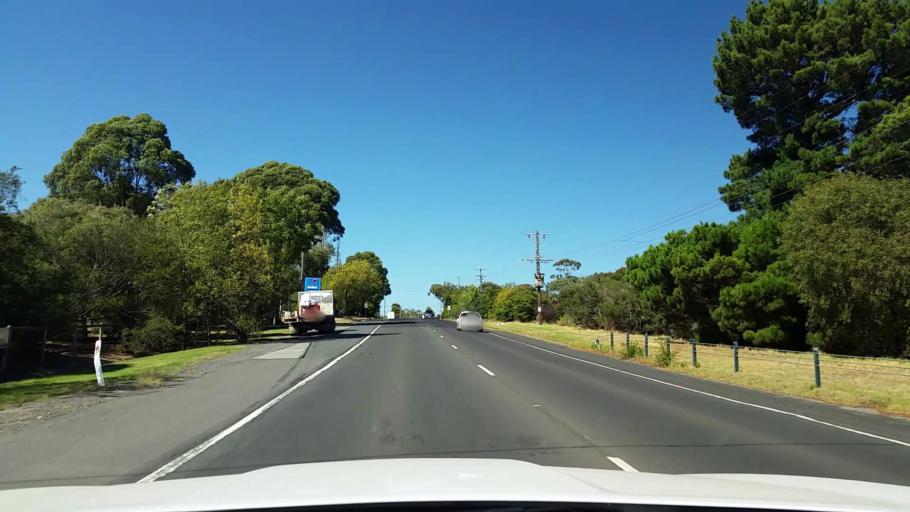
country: AU
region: Victoria
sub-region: Mornington Peninsula
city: Somerville
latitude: -38.2204
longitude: 145.1732
